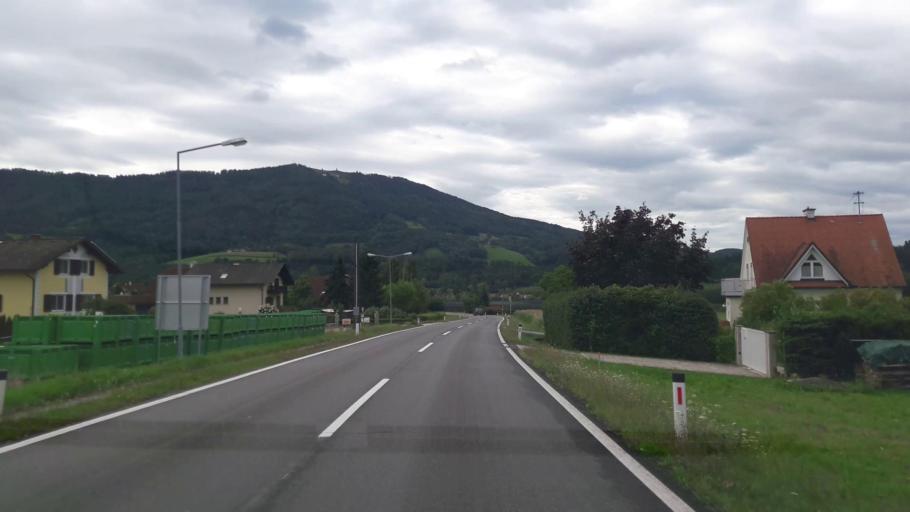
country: AT
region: Styria
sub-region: Politischer Bezirk Weiz
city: Floing
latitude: 47.2470
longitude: 15.7313
